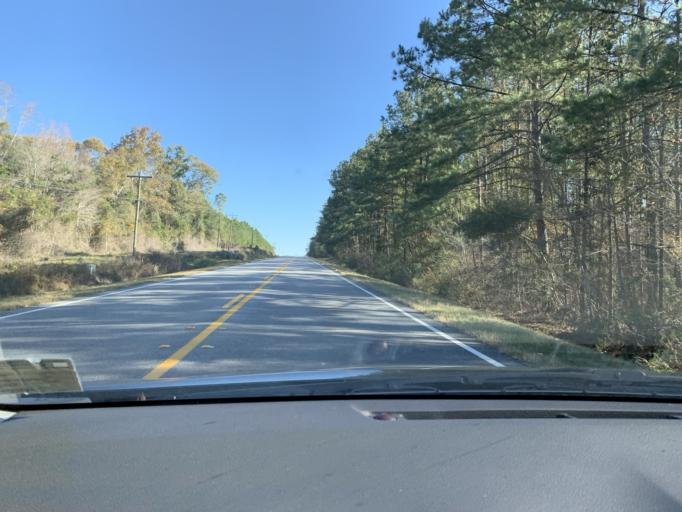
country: US
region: Georgia
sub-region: Ben Hill County
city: Fitzgerald
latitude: 31.7678
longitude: -83.1048
